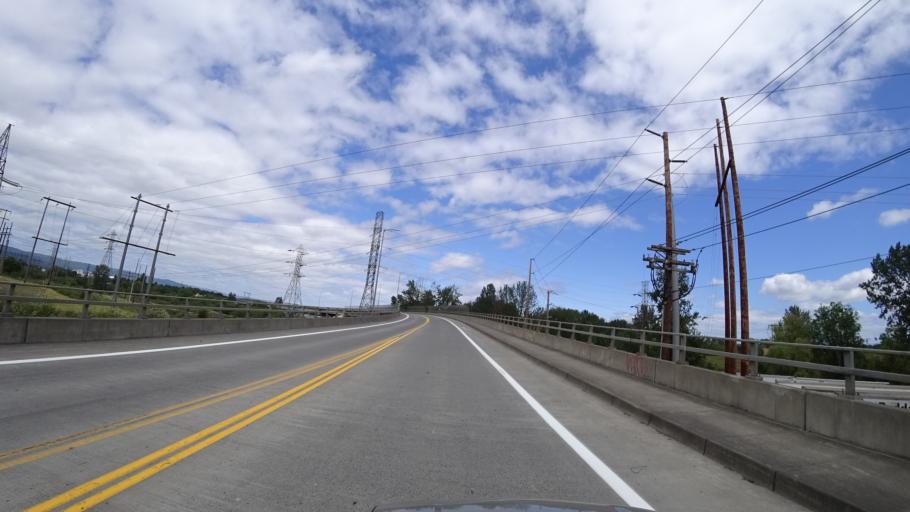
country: US
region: Oregon
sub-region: Washington County
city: West Haven
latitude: 45.6141
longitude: -122.7630
